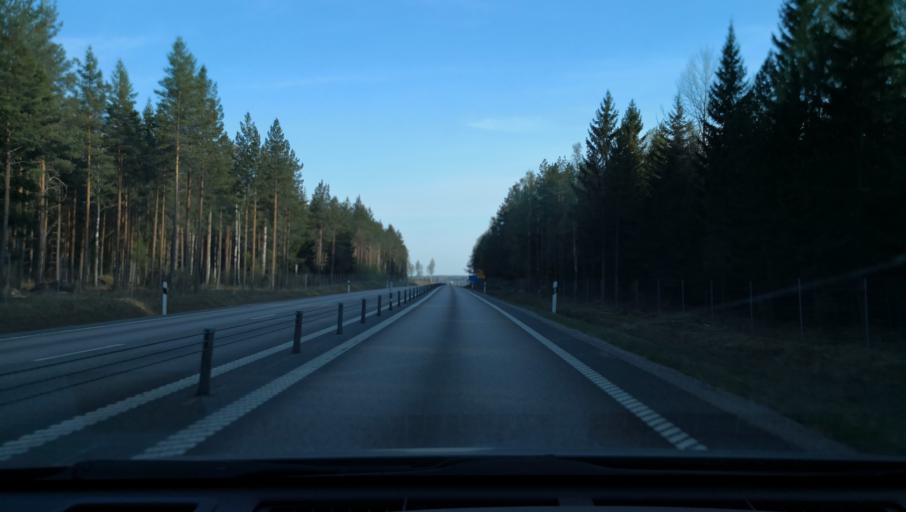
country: SE
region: Uppsala
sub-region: Heby Kommun
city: Heby
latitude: 59.9634
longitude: 16.8360
